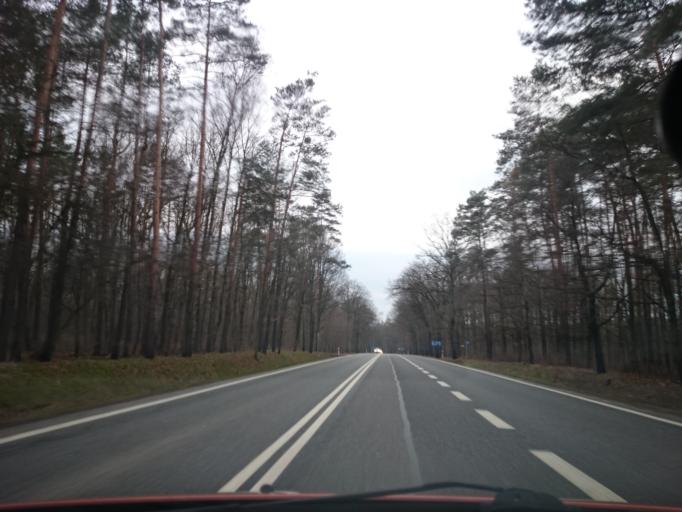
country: PL
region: Opole Voivodeship
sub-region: Powiat opolski
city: Dabrowa
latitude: 50.6876
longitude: 17.7351
